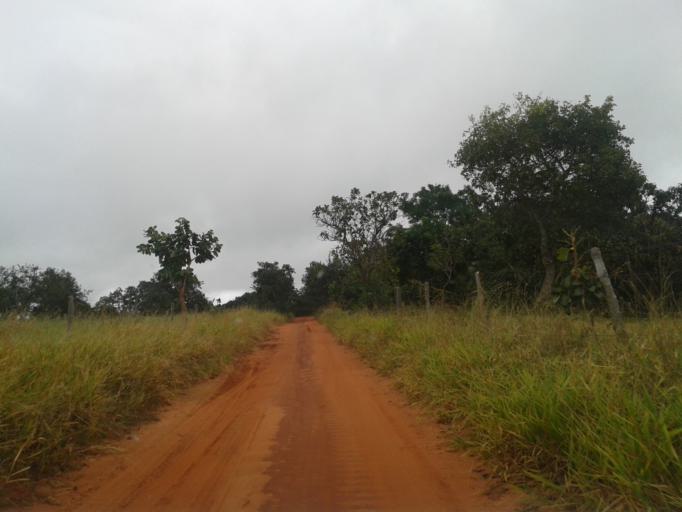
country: BR
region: Minas Gerais
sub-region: Campina Verde
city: Campina Verde
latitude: -19.3957
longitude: -49.6171
